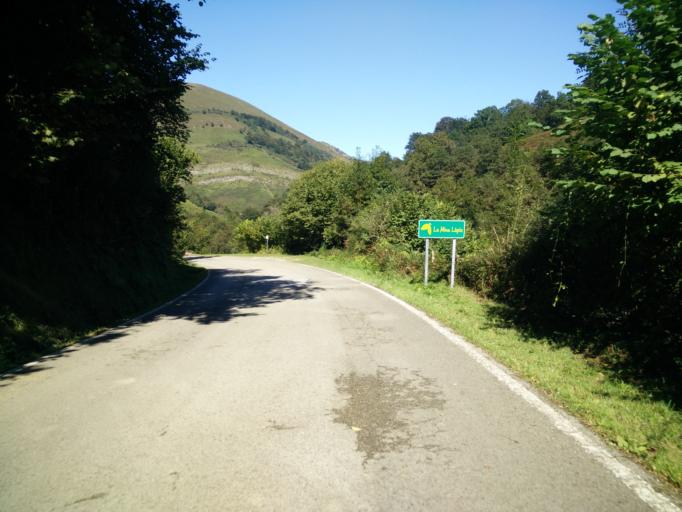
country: ES
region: Cantabria
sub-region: Provincia de Cantabria
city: Ruente
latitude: 43.1223
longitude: -4.2952
